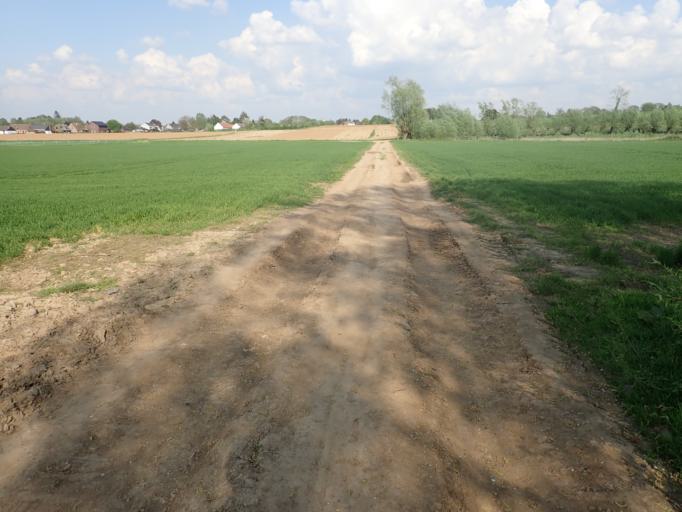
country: BE
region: Flanders
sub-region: Provincie Vlaams-Brabant
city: Bever
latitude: 50.9361
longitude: 4.2936
